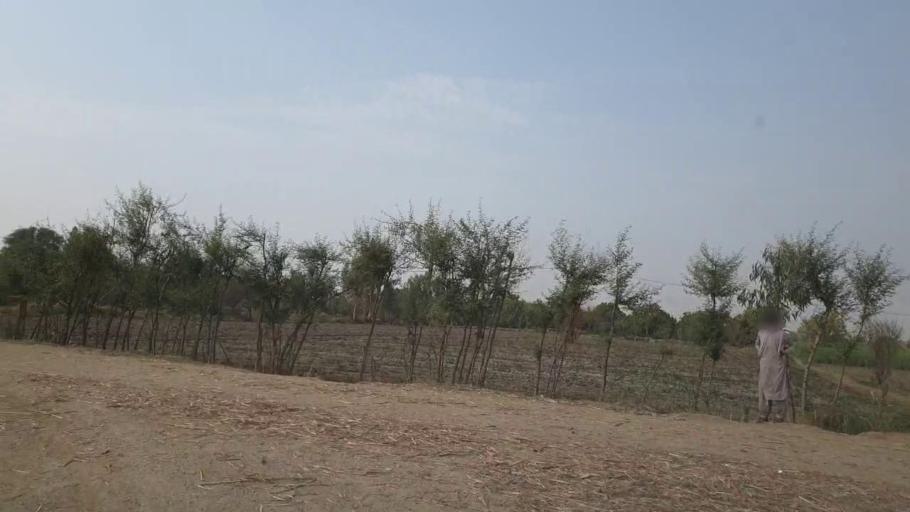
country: PK
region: Sindh
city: Mirpur Khas
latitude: 25.5805
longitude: 69.1349
